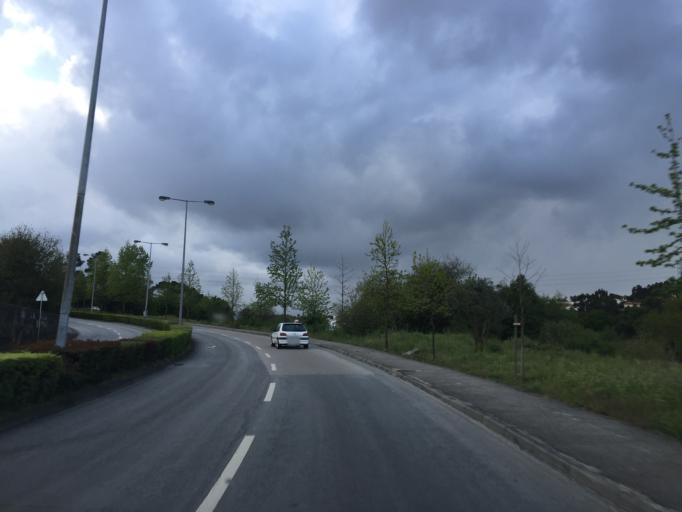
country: PT
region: Viseu
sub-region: Viseu
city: Viseu
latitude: 40.6628
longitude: -7.9225
